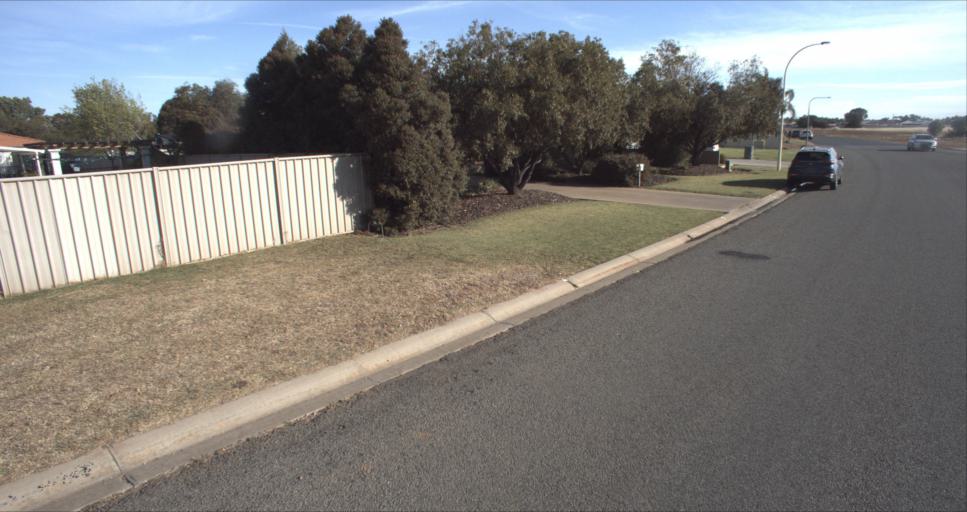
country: AU
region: New South Wales
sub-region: Leeton
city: Leeton
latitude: -34.5410
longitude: 146.4009
